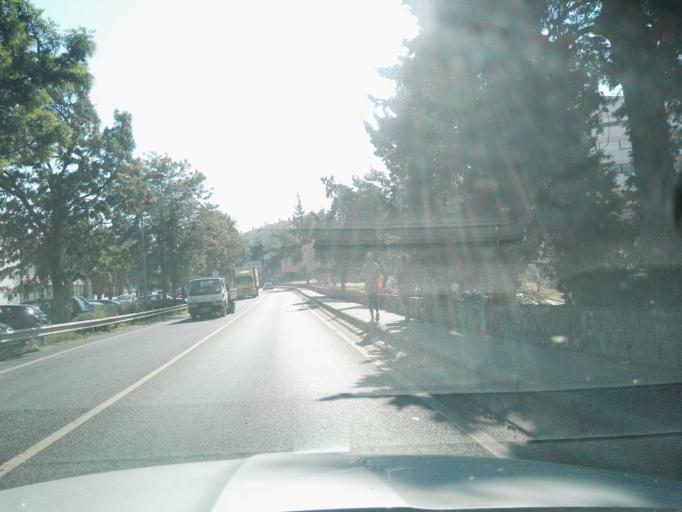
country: PT
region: Lisbon
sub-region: Vila Franca de Xira
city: Vialonga
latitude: 38.8708
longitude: -9.0561
